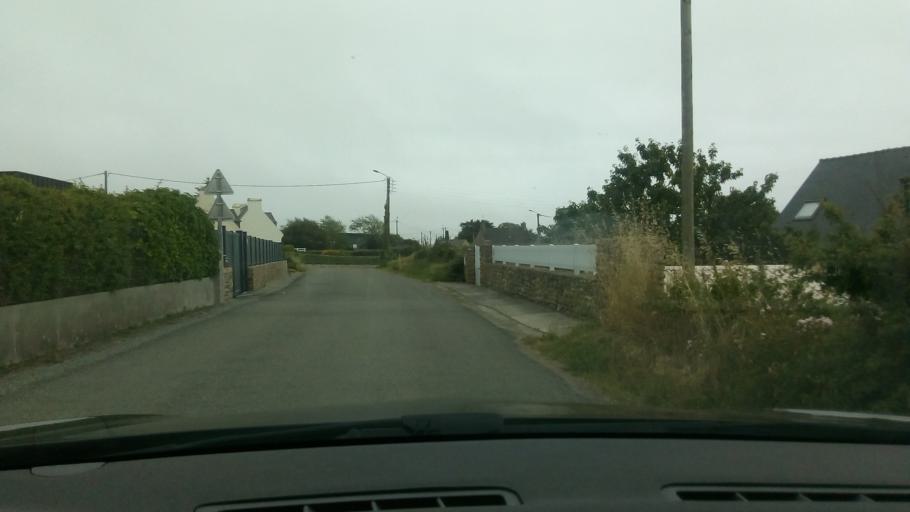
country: FR
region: Brittany
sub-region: Departement du Finistere
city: Le Conquet
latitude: 48.3538
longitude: -4.7714
